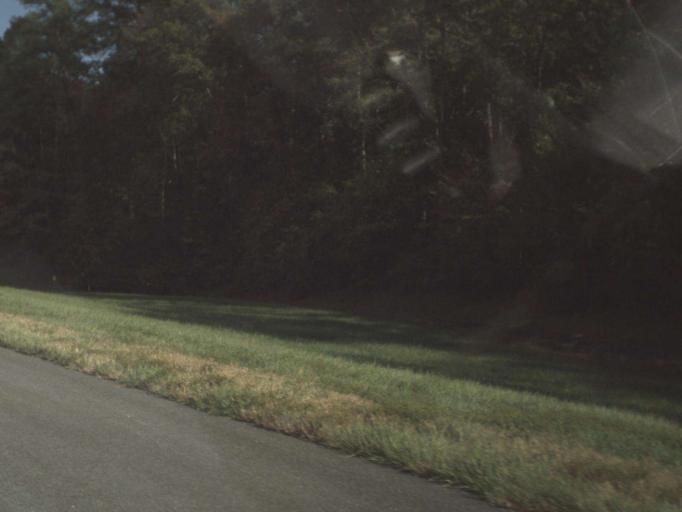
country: US
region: Florida
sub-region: Gadsden County
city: Chattahoochee
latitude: 30.6306
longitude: -84.8791
